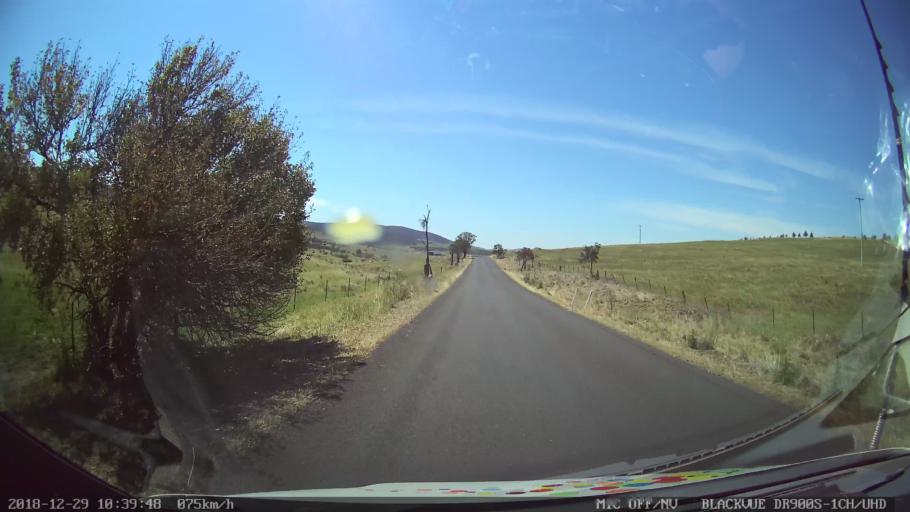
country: AU
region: New South Wales
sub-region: Palerang
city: Bungendore
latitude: -35.0101
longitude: 149.5124
